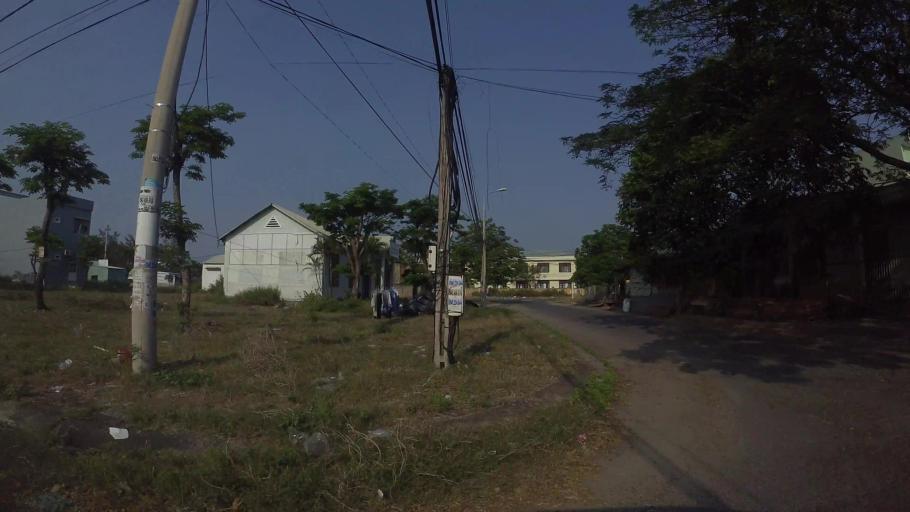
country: VN
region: Da Nang
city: Ngu Hanh Son
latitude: 15.9557
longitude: 108.2564
